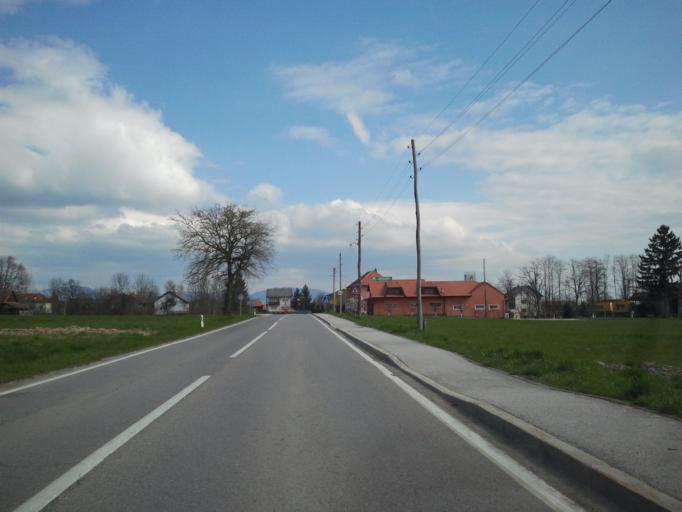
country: HR
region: Zagrebacka
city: Jastrebarsko
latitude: 45.5888
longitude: 15.5971
